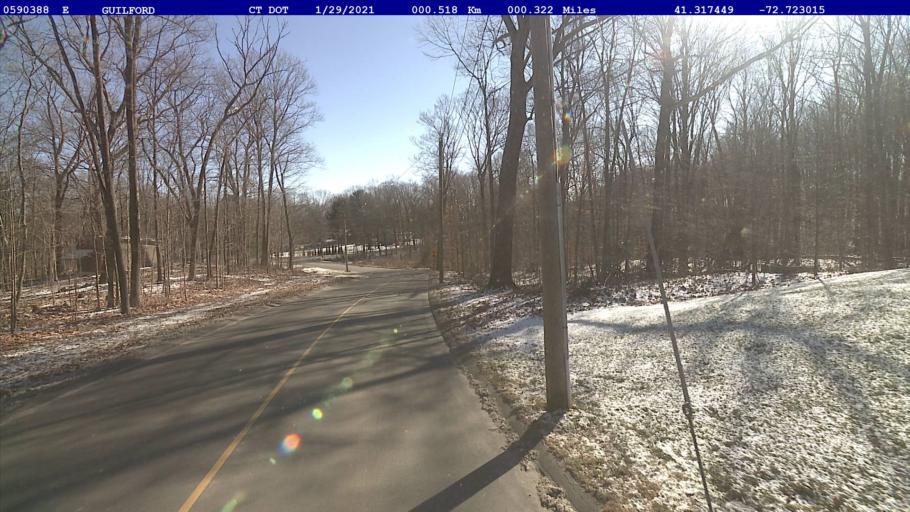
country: US
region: Connecticut
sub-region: New Haven County
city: North Branford
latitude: 41.3174
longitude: -72.7230
